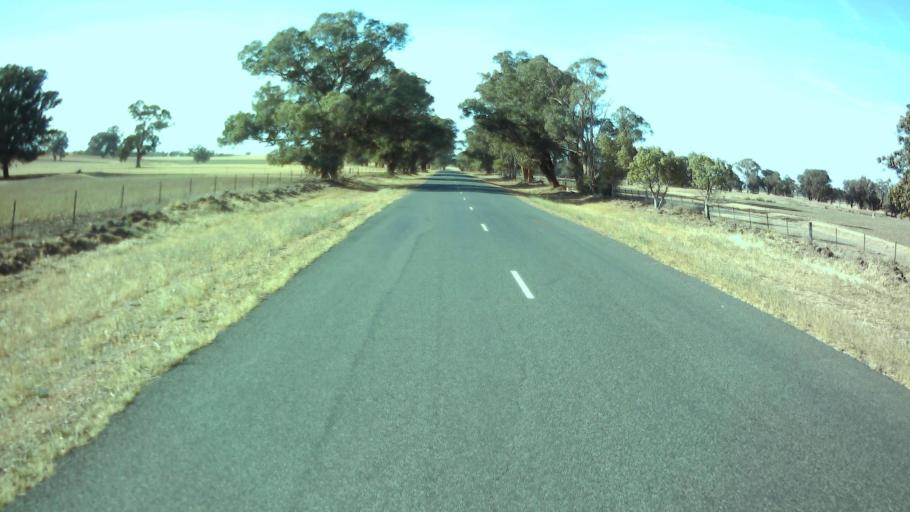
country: AU
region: New South Wales
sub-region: Weddin
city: Grenfell
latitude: -33.9600
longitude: 148.1399
